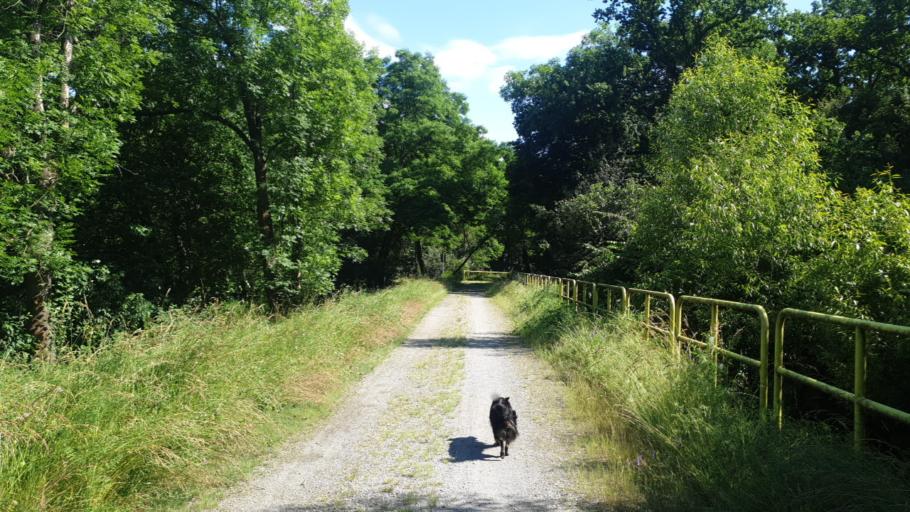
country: PL
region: Lower Silesian Voivodeship
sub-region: Powiat wroclawski
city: Radwanice
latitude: 51.0859
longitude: 17.1173
